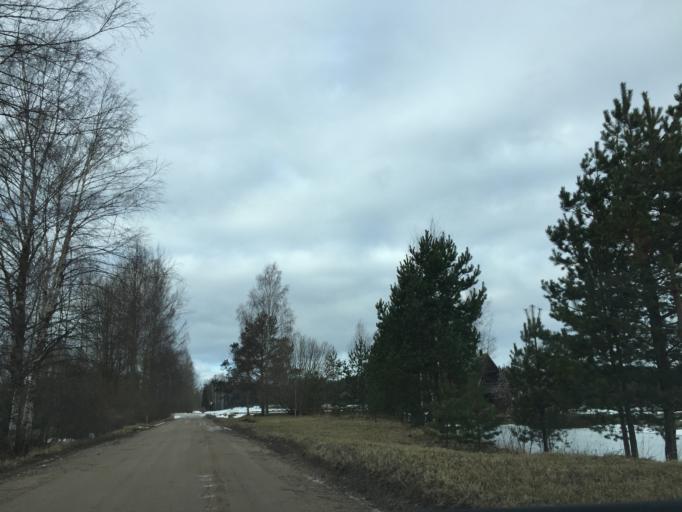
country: LV
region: Salacgrivas
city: Ainazi
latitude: 57.8484
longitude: 24.4863
